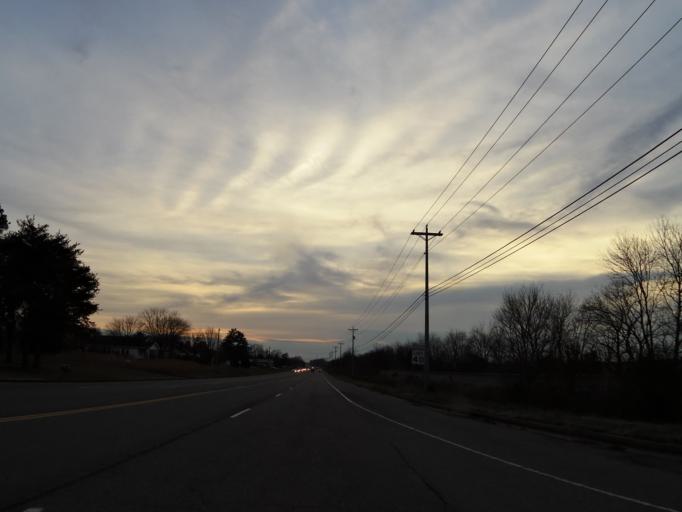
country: US
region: Tennessee
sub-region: McMinn County
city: Englewood
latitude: 35.4366
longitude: -84.4679
